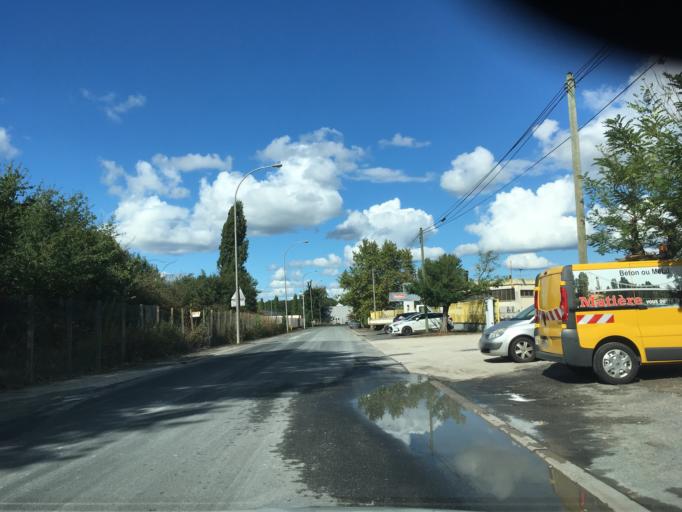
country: FR
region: Limousin
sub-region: Departement de la Correze
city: Saint-Pantaleon-de-Larche
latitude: 45.1507
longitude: 1.4779
